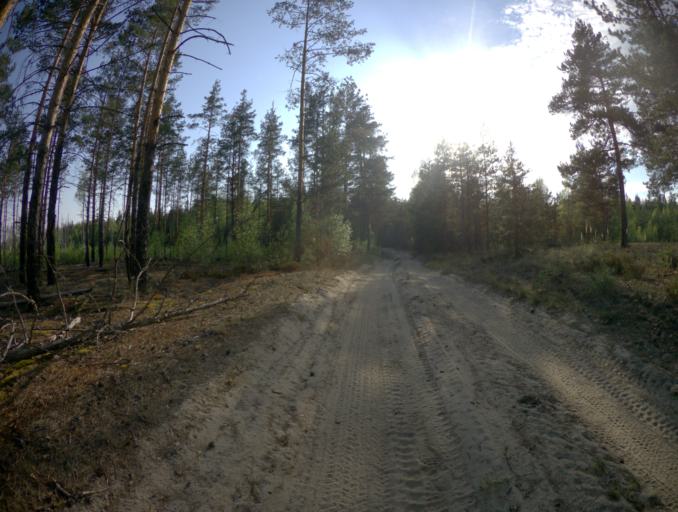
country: RU
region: Vladimir
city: Vyazniki
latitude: 56.4030
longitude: 42.1732
